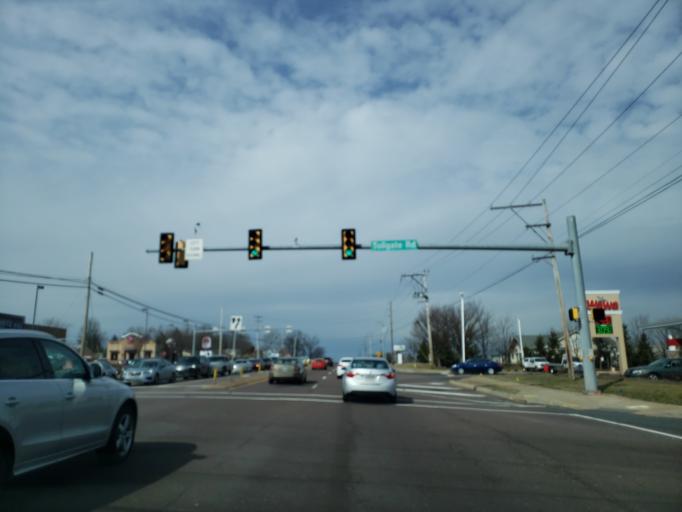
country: US
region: Pennsylvania
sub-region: Bucks County
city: Quakertown
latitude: 40.4172
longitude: -75.3438
